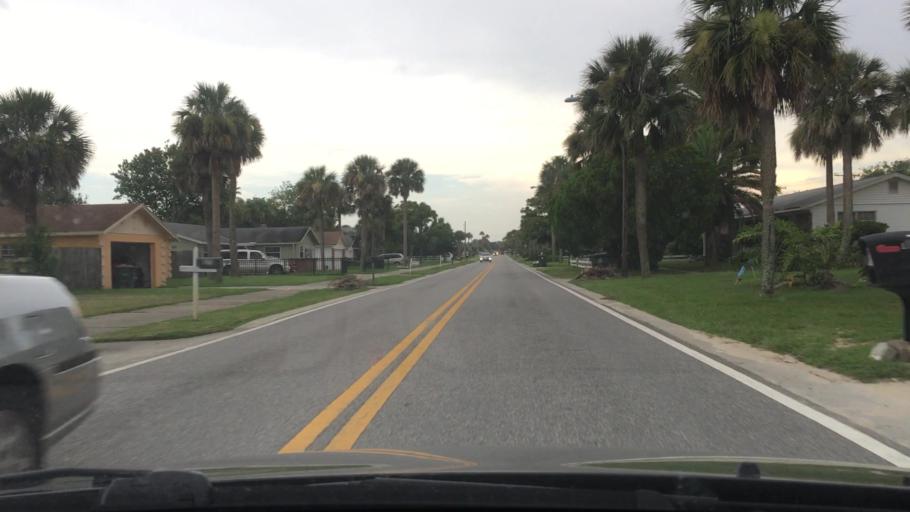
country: US
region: Florida
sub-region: Volusia County
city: Holly Hill
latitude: 29.2250
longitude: -81.0605
